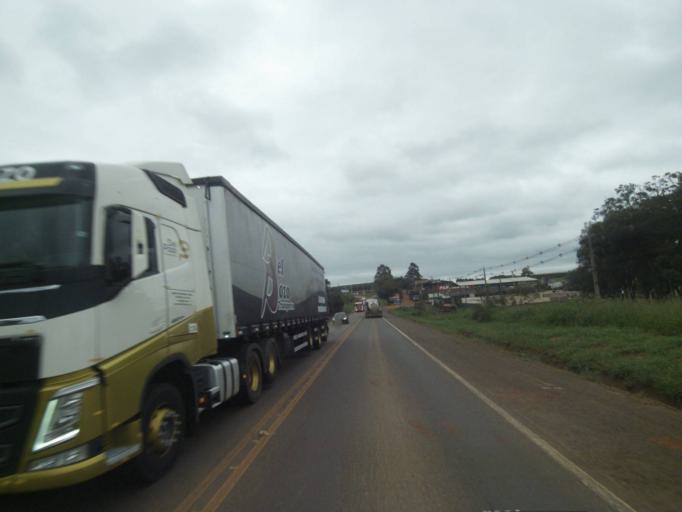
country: BR
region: Parana
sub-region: Telemaco Borba
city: Telemaco Borba
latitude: -24.3821
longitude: -50.6724
